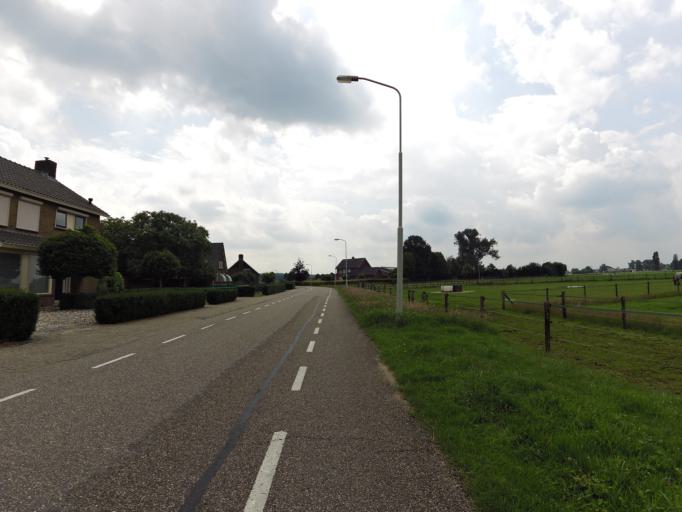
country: NL
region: Gelderland
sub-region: Gemeente Montferland
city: s-Heerenberg
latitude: 51.9292
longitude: 6.2057
